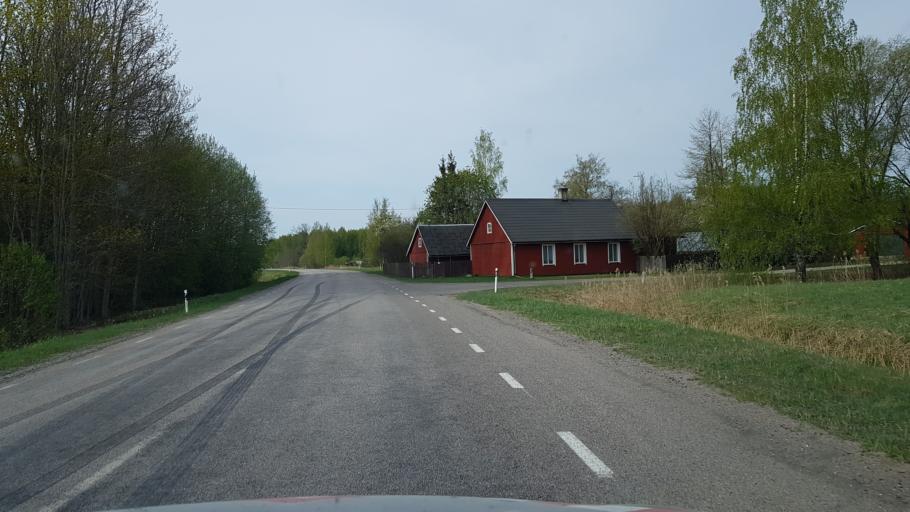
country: EE
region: Paernumaa
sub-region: Audru vald
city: Audru
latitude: 58.3921
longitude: 24.2779
